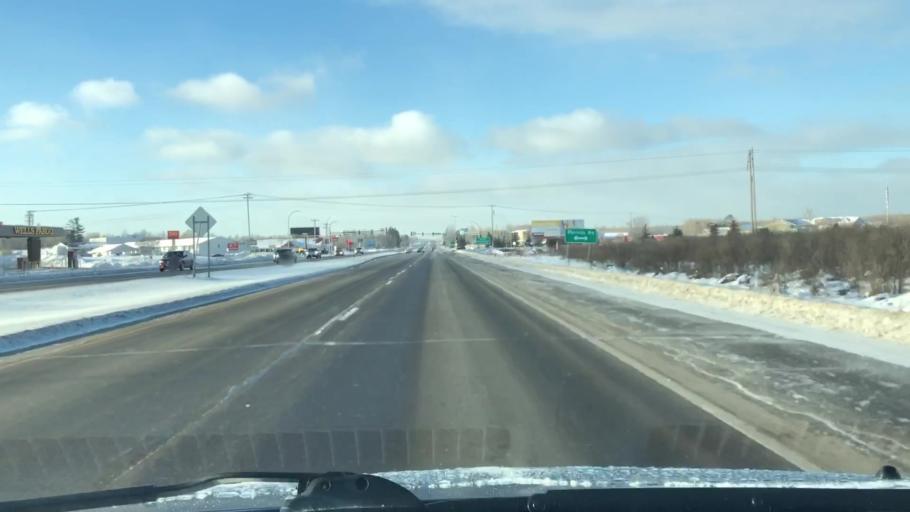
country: US
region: Minnesota
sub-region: Saint Louis County
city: Hermantown
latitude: 46.8133
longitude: -92.1721
